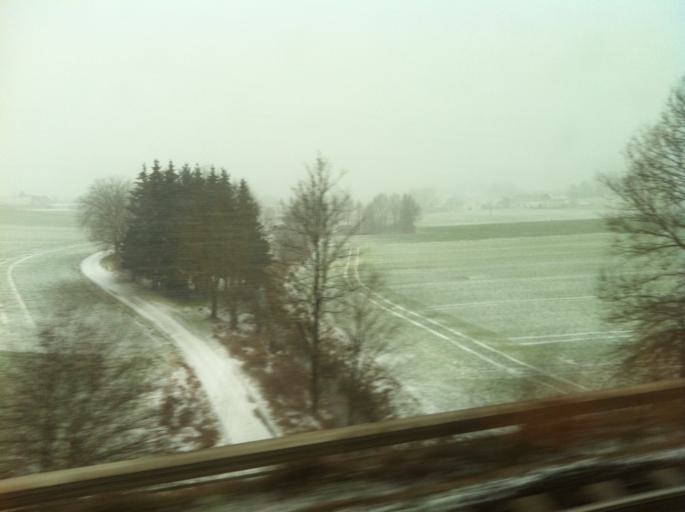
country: DE
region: Bavaria
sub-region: Swabia
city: Dinkelscherben
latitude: 48.3496
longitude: 10.5661
